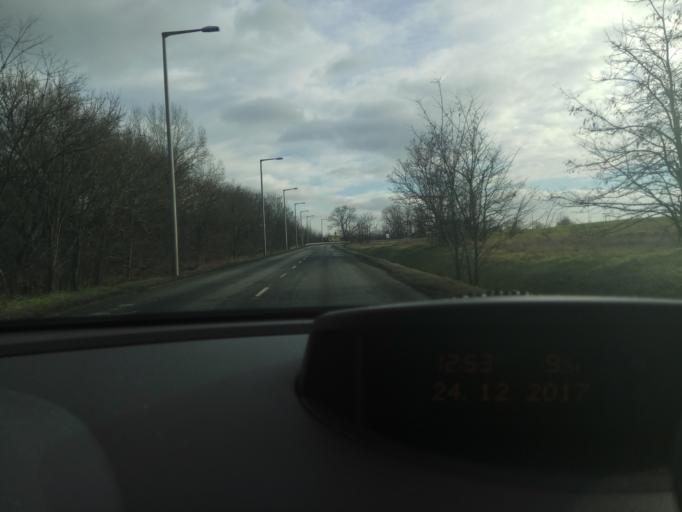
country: HU
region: Budapest
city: Budapest XV. keruelet
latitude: 47.5793
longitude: 19.1421
